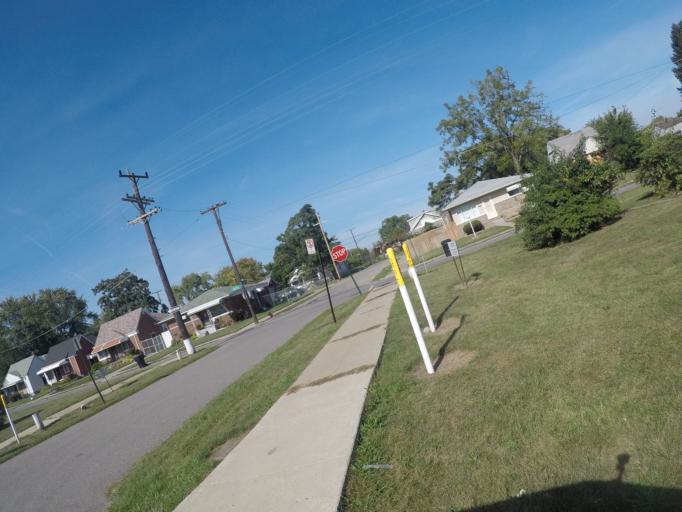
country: US
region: Michigan
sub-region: Wayne County
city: Lincoln Park
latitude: 42.2619
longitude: -83.1644
